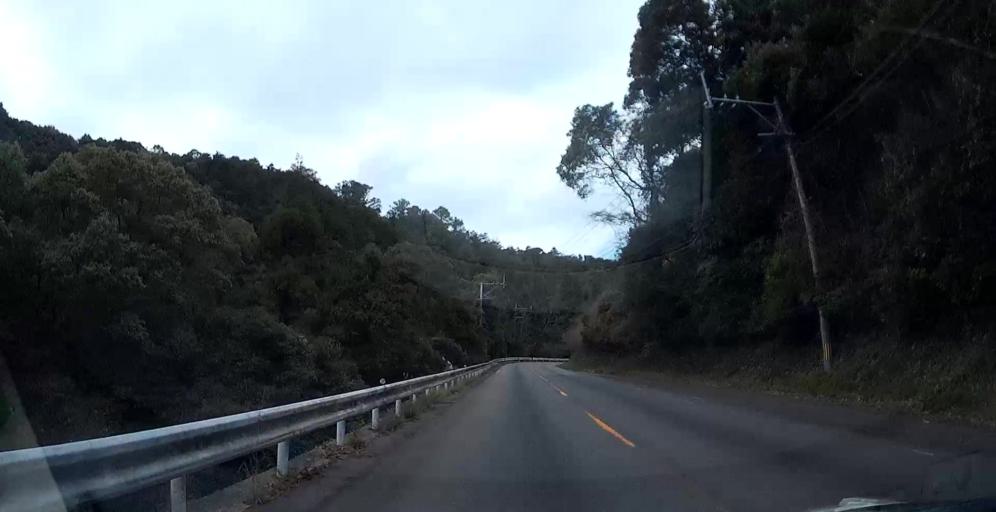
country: JP
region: Kumamoto
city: Yatsushiro
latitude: 32.3686
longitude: 130.5053
